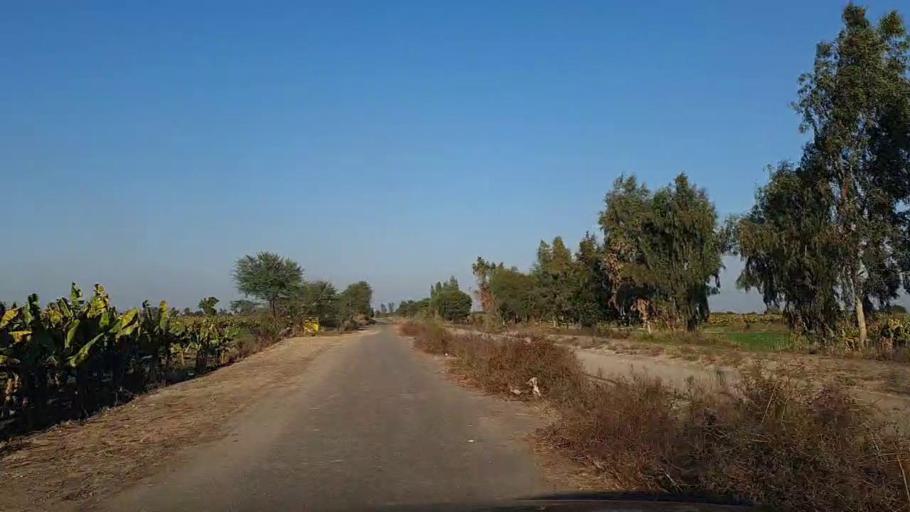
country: PK
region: Sindh
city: Sakrand
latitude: 26.2313
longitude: 68.2764
